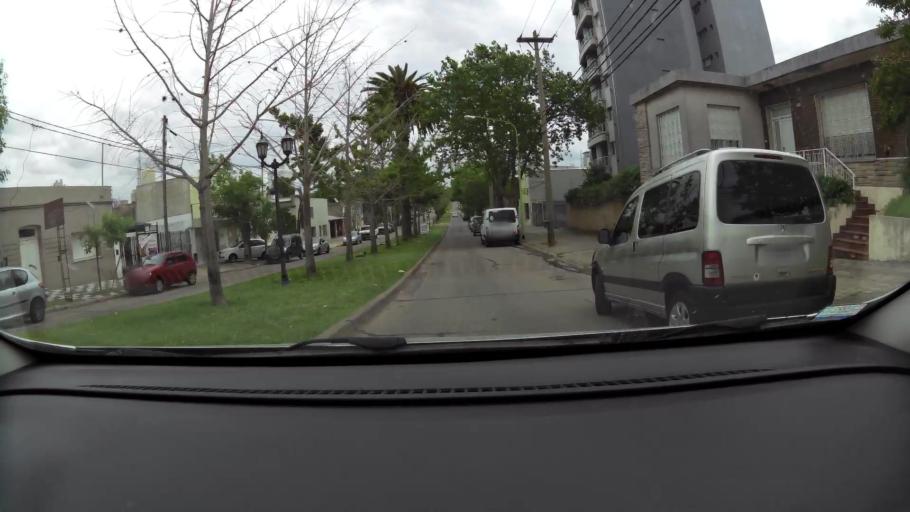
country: AR
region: Buenos Aires
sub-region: Partido de Campana
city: Campana
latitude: -34.1636
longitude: -58.9536
